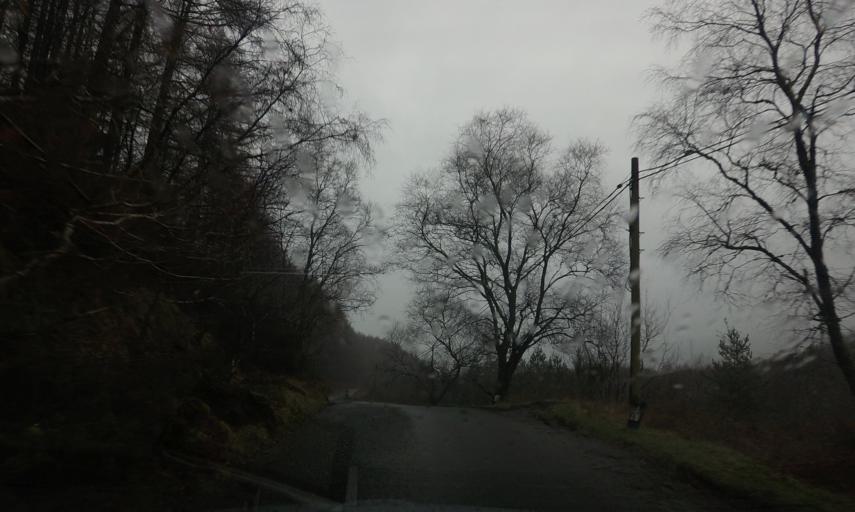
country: GB
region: Scotland
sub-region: West Dunbartonshire
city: Balloch
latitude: 56.1427
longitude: -4.6356
